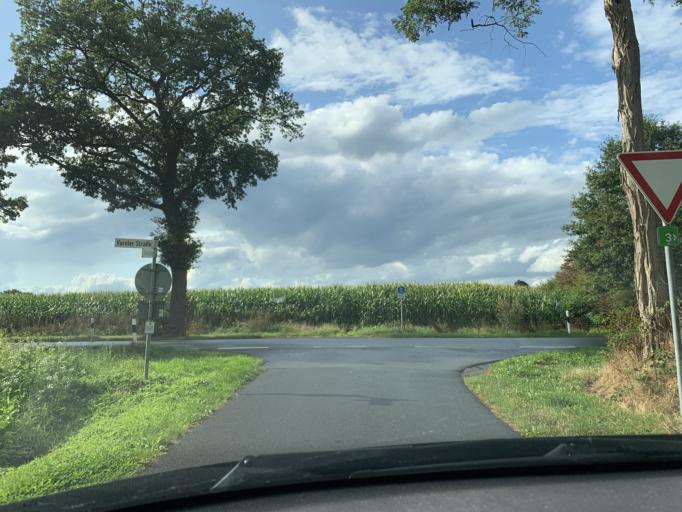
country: DE
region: Lower Saxony
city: Westerstede
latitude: 53.3065
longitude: 7.9999
